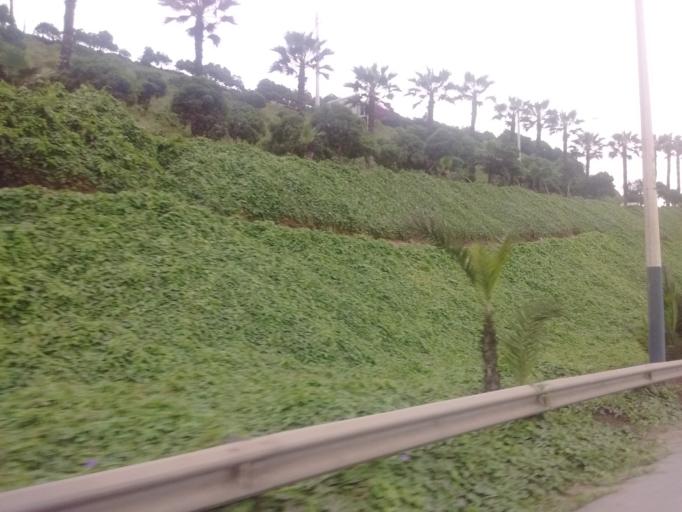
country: PE
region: Lima
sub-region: Lima
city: San Isidro
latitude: -12.1094
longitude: -77.0566
